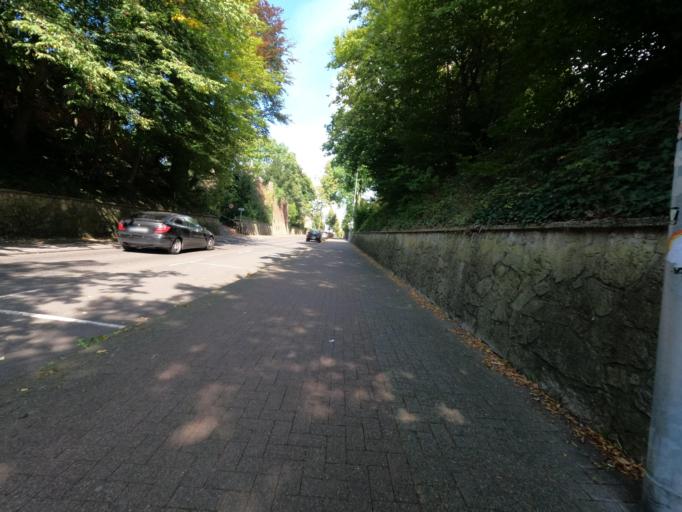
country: DE
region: North Rhine-Westphalia
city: Geilenkirchen
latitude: 50.9664
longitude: 6.1195
